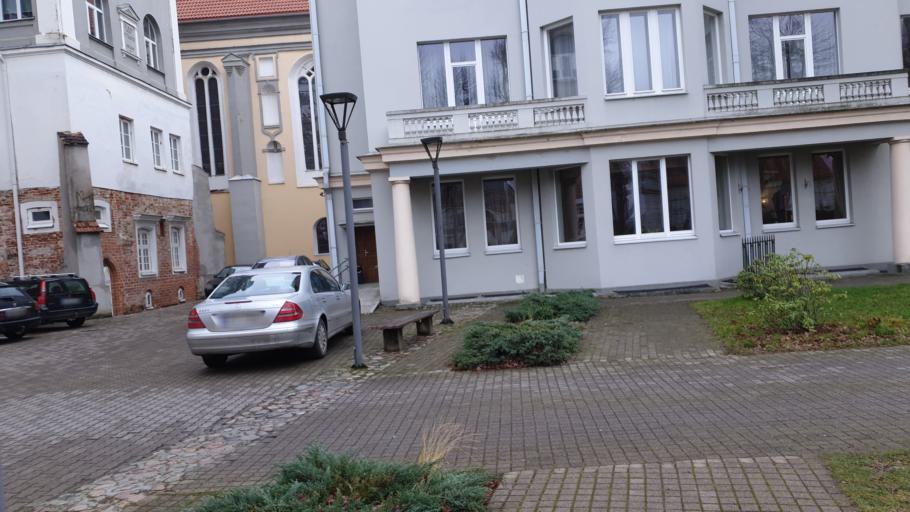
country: LT
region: Kauno apskritis
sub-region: Kaunas
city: Kaunas
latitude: 54.8978
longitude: 23.8842
